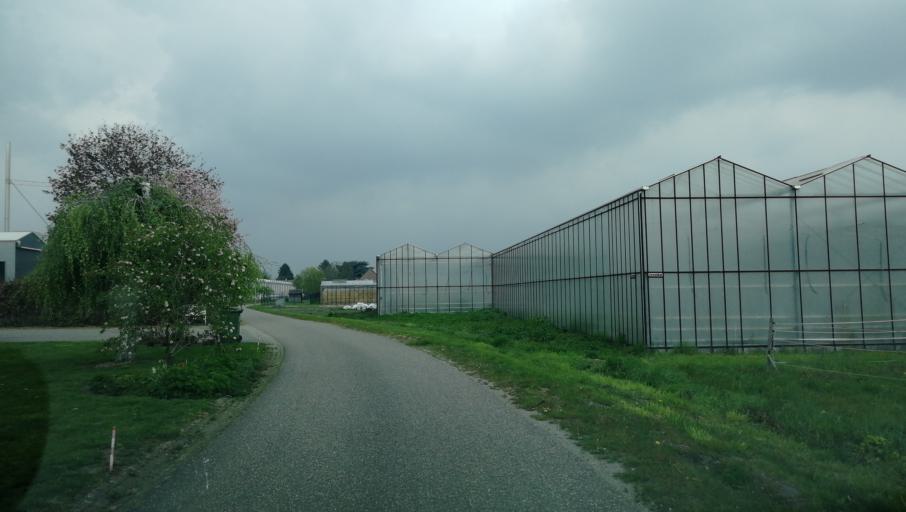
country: NL
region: Limburg
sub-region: Gemeente Venlo
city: Venlo
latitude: 51.3895
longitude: 6.2084
